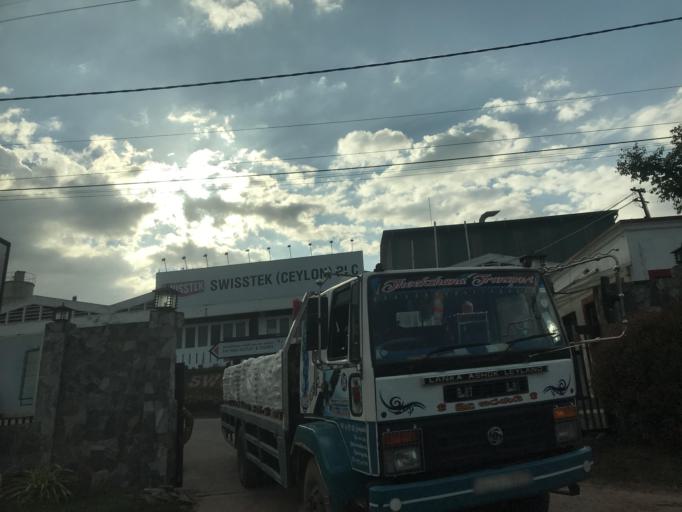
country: LK
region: Western
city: Gampaha
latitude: 7.0563
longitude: 80.0084
